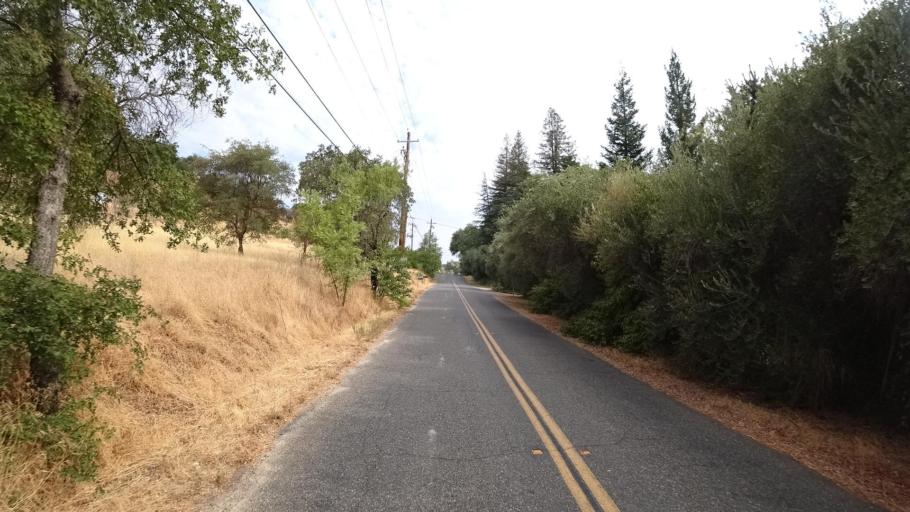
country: US
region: California
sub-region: Placer County
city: Loomis
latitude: 38.8314
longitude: -121.2195
